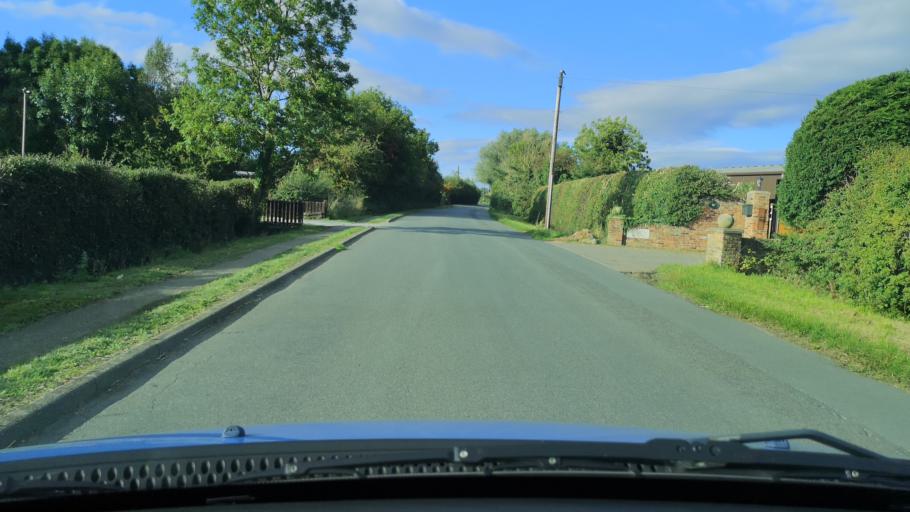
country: GB
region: England
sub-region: Doncaster
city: Stainforth
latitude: 53.6178
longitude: -1.0136
